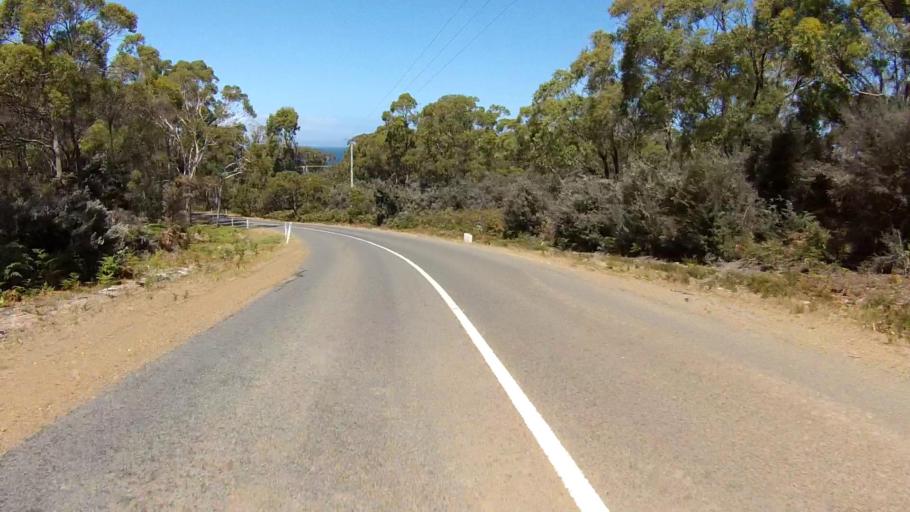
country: AU
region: Tasmania
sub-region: Clarence
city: Sandford
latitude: -43.0244
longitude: 147.4811
